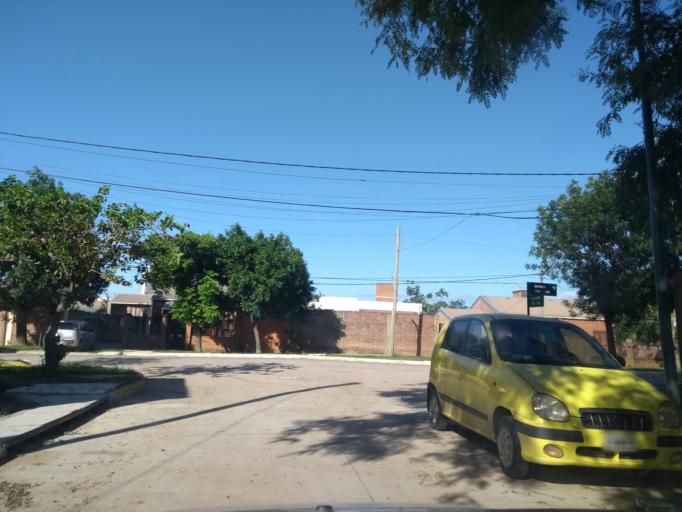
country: AR
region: Chaco
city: Resistencia
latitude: -27.4743
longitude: -58.9806
